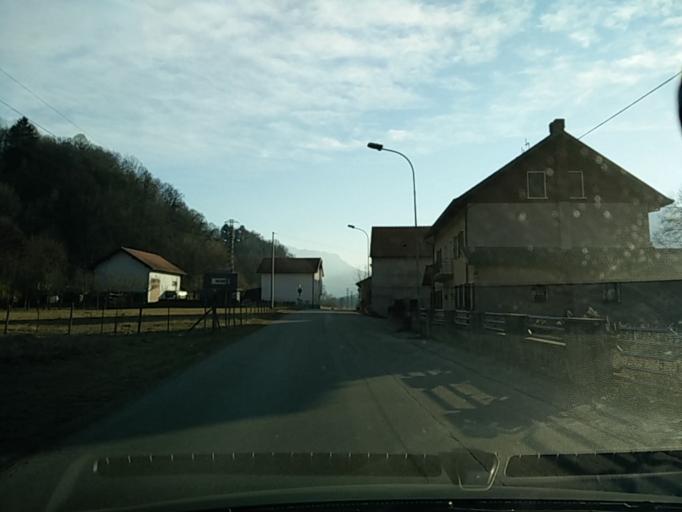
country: IT
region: Veneto
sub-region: Provincia di Belluno
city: Puos d'Alpago
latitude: 46.1414
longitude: 12.3297
